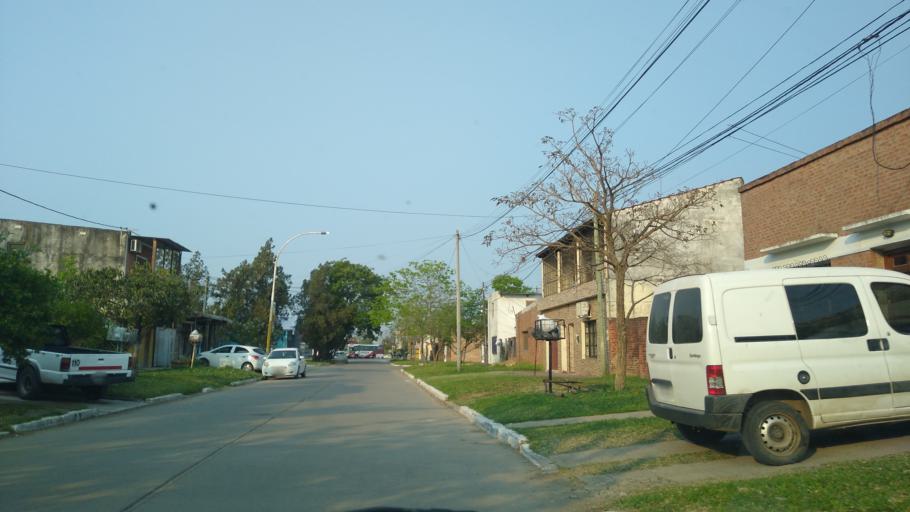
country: AR
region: Chaco
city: Barranqueras
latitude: -27.4820
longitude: -58.9439
